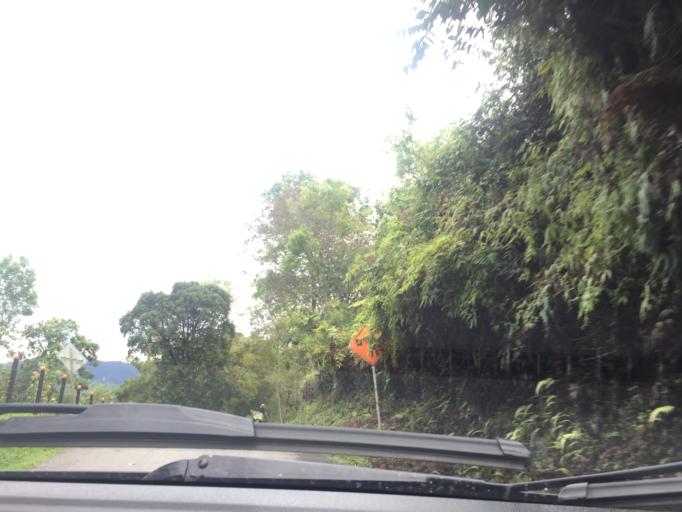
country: CO
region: Cundinamarca
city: Supata
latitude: 5.0539
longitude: -74.2360
